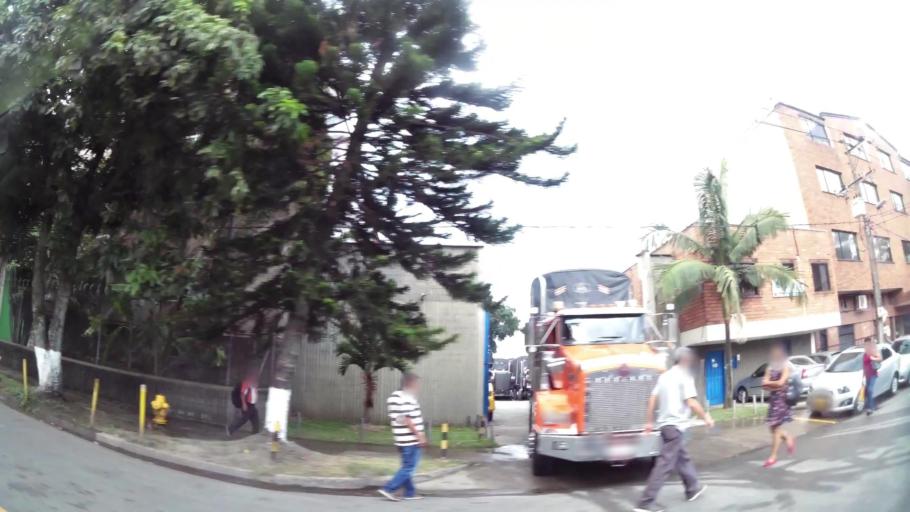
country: CO
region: Antioquia
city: Itagui
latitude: 6.1993
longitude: -75.5878
